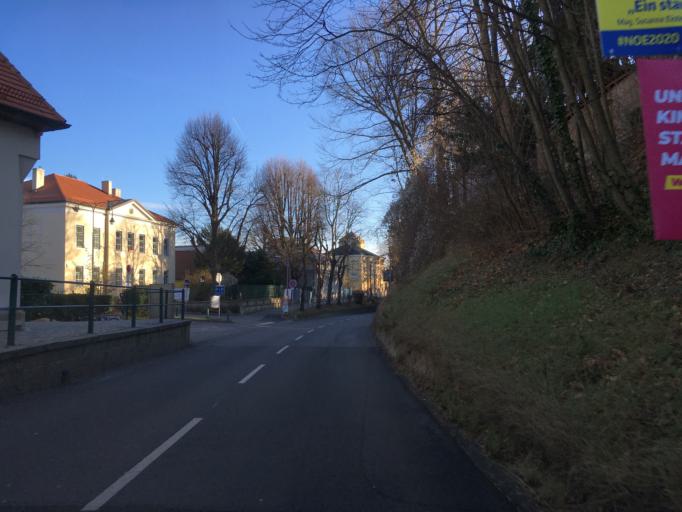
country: AT
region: Lower Austria
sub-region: Politischer Bezirk Wien-Umgebung
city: Klosterneuburg
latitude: 48.3276
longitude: 16.3018
